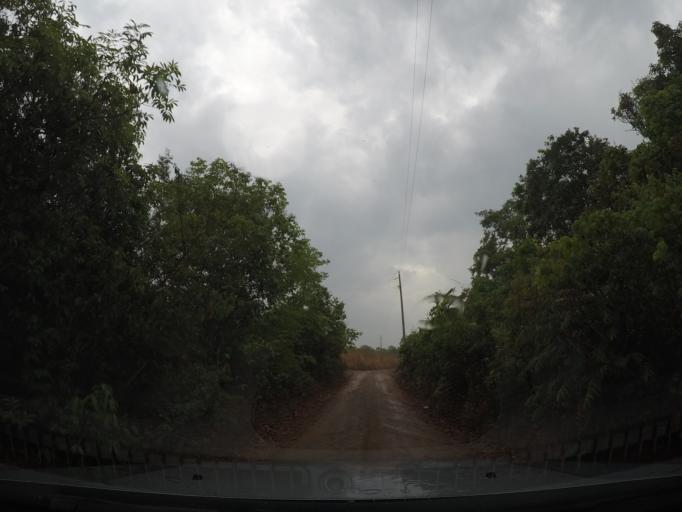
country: BR
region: Goias
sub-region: Pirenopolis
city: Pirenopolis
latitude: -15.8303
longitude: -48.8849
